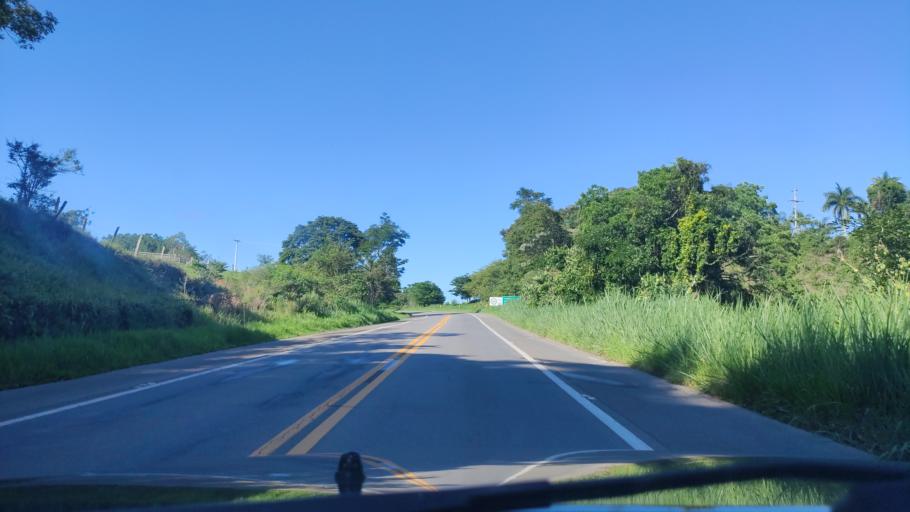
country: BR
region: Sao Paulo
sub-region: Socorro
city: Socorro
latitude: -22.5524
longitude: -46.5818
